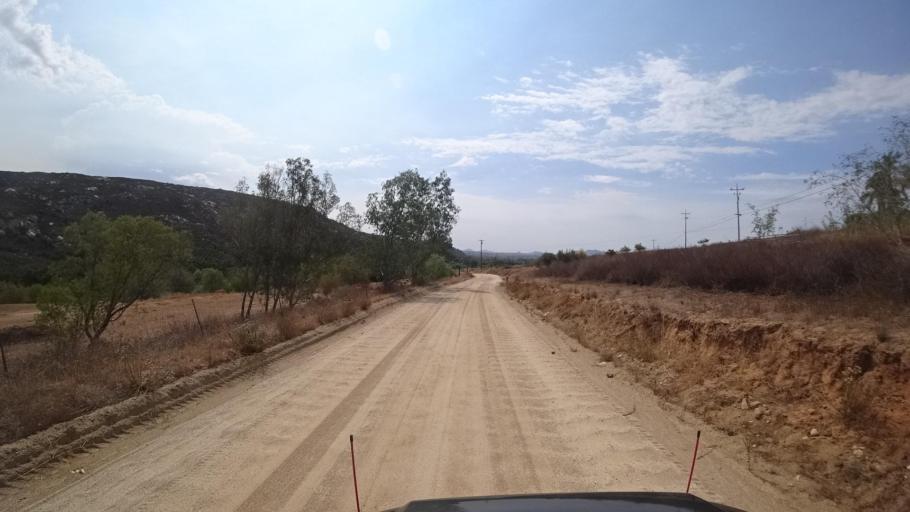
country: US
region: California
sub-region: San Diego County
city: Ramona
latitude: 33.0924
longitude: -116.8313
